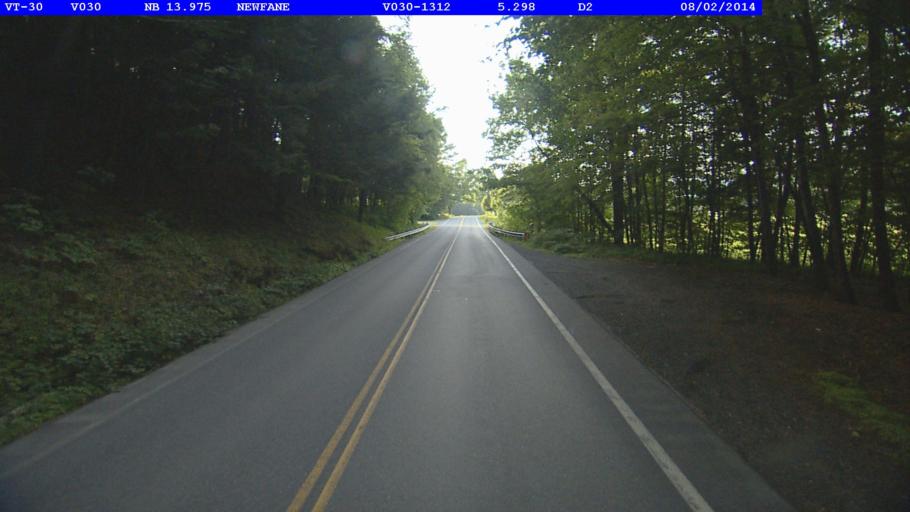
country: US
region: Vermont
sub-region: Windham County
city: Newfane
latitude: 43.0152
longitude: -72.6525
